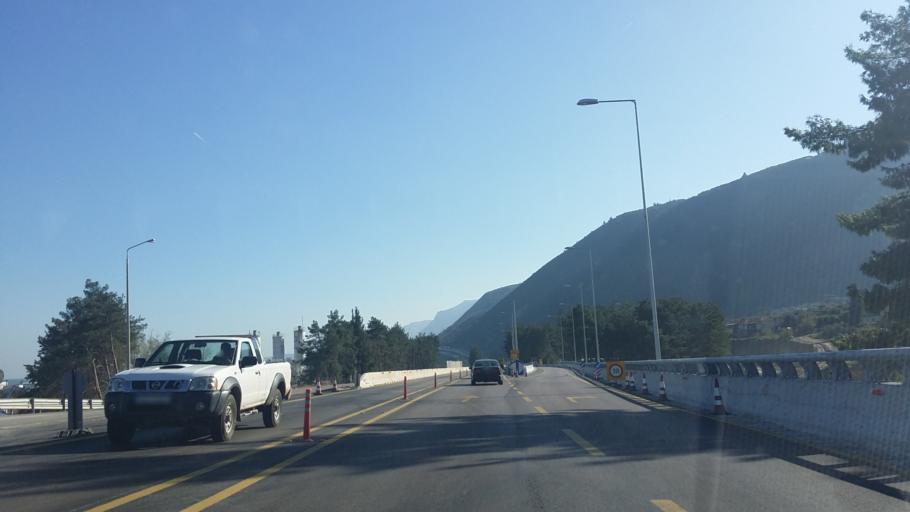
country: GR
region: West Greece
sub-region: Nomos Achaias
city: Temeni
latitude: 38.2222
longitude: 22.1009
